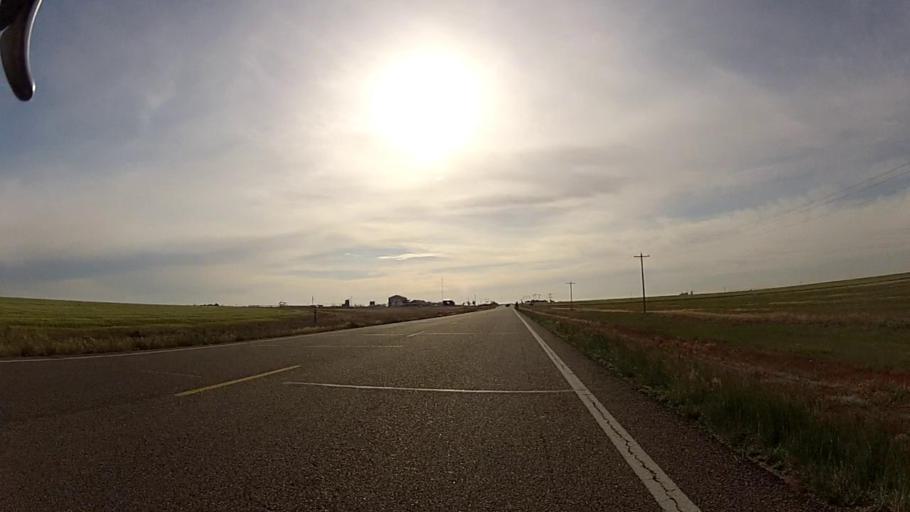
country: US
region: Kansas
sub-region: Grant County
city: Ulysses
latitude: 37.5767
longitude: -101.4942
